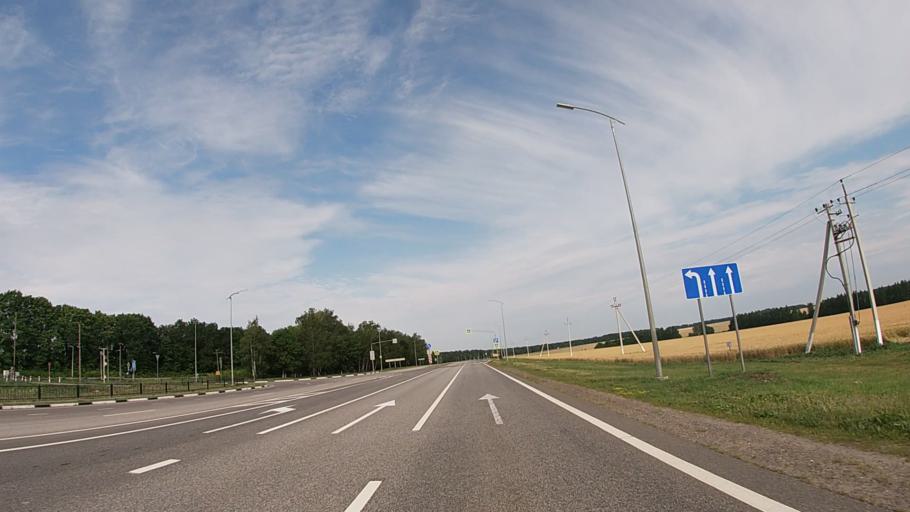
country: RU
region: Belgorod
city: Borisovka
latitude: 50.7503
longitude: 35.9843
